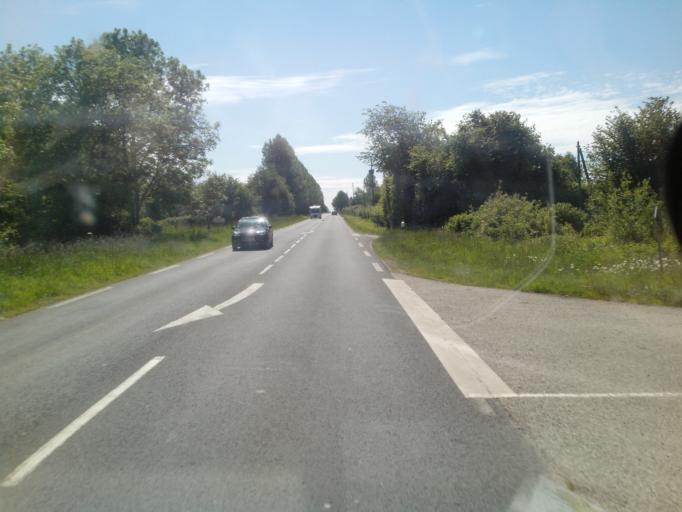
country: FR
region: Haute-Normandie
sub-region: Departement de l'Eure
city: Beuzeville
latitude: 49.3239
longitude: 0.2858
